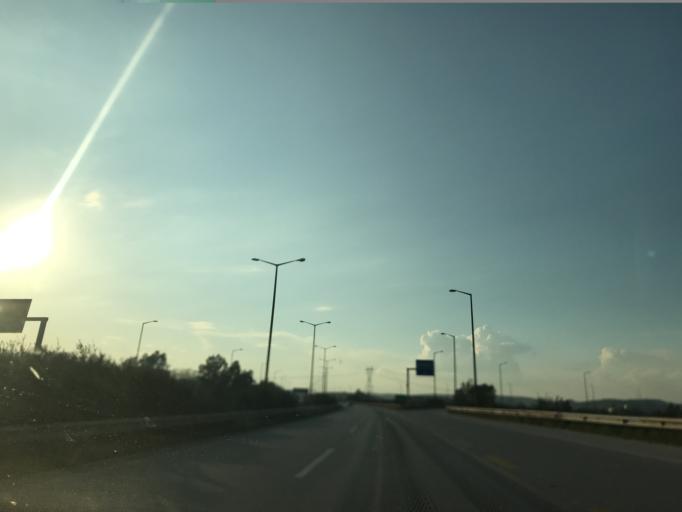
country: TR
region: Osmaniye
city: Toprakkale
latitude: 36.9749
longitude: 36.0193
